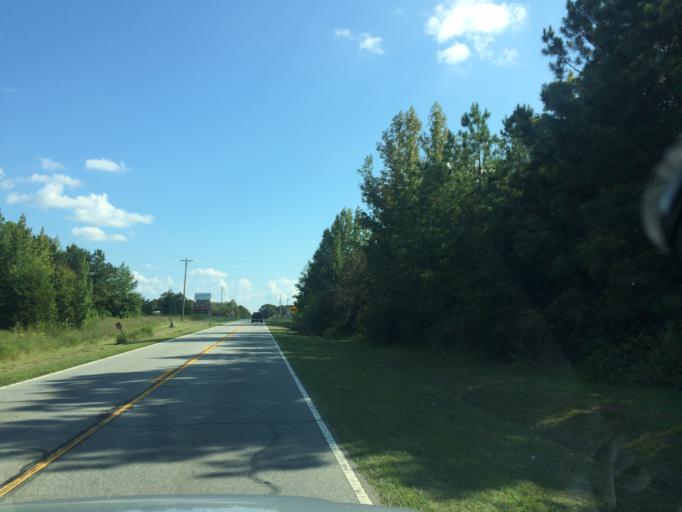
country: US
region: South Carolina
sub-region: Greenville County
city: Fountain Inn
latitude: 34.5981
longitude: -82.1069
